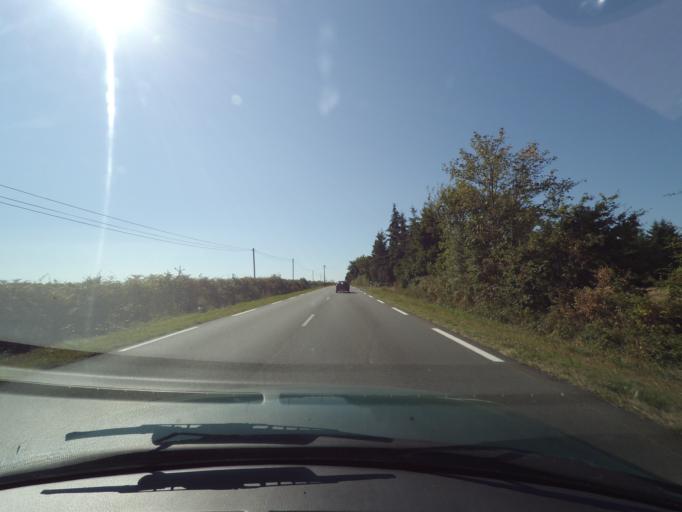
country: FR
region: Poitou-Charentes
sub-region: Departement de la Vienne
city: Saulge
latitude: 46.3175
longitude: 0.8238
